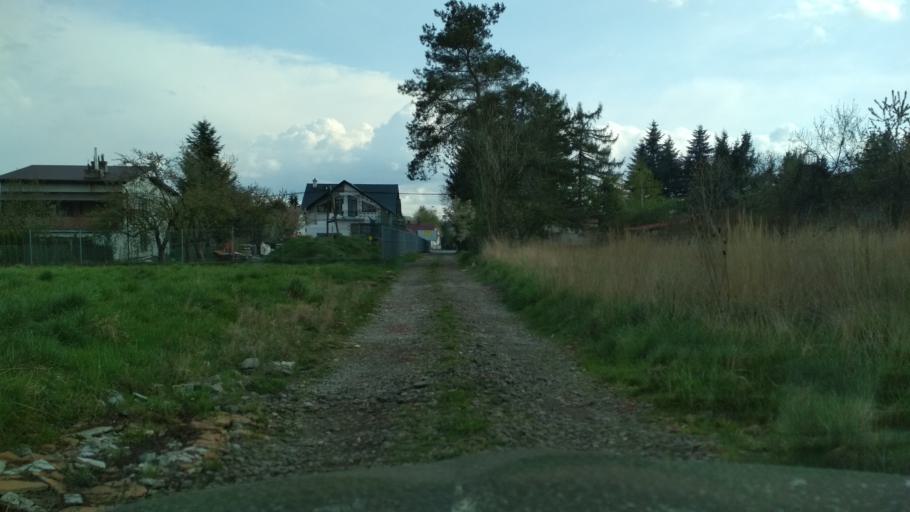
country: PL
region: Subcarpathian Voivodeship
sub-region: Powiat rzeszowski
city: Rudna Wielka
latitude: 50.0617
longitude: 21.9500
